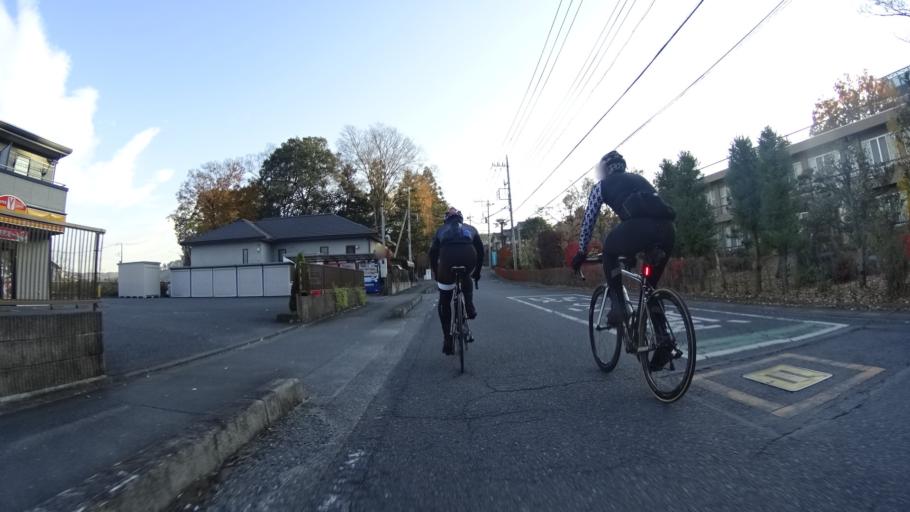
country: JP
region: Saitama
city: Hanno
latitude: 35.8406
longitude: 139.3185
